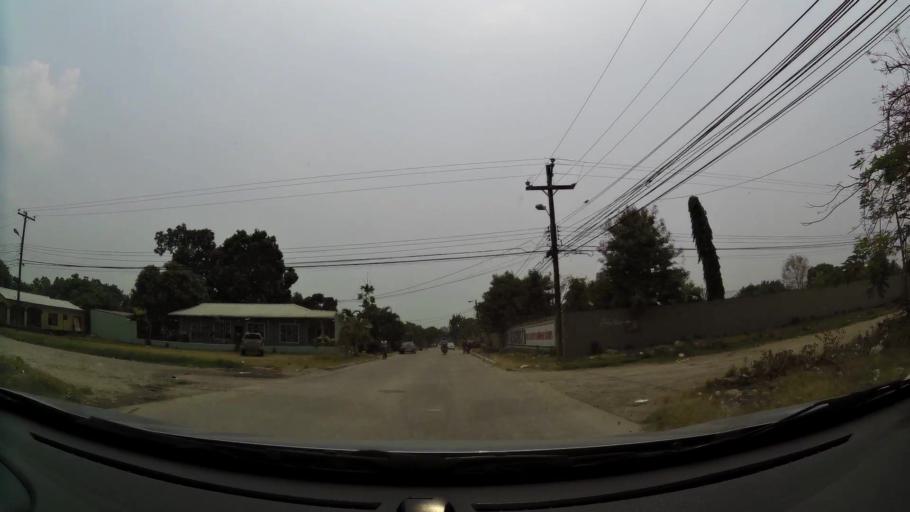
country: HN
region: Yoro
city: El Progreso
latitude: 15.3882
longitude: -87.7971
